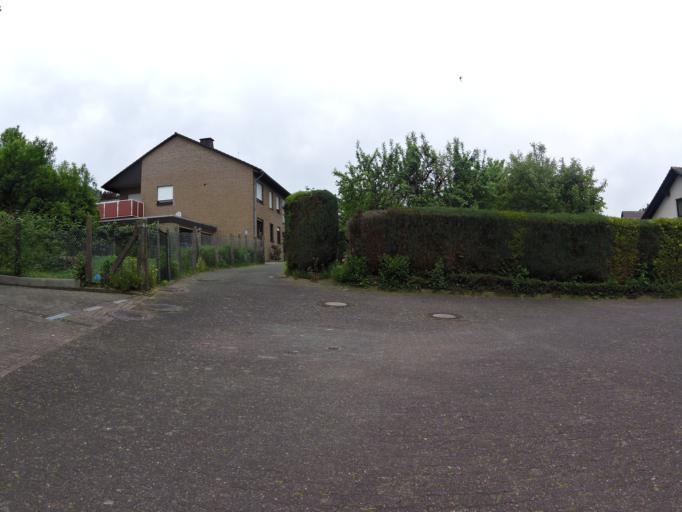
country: DE
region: North Rhine-Westphalia
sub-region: Regierungsbezirk Detmold
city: Hoexter
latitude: 51.7775
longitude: 9.3727
